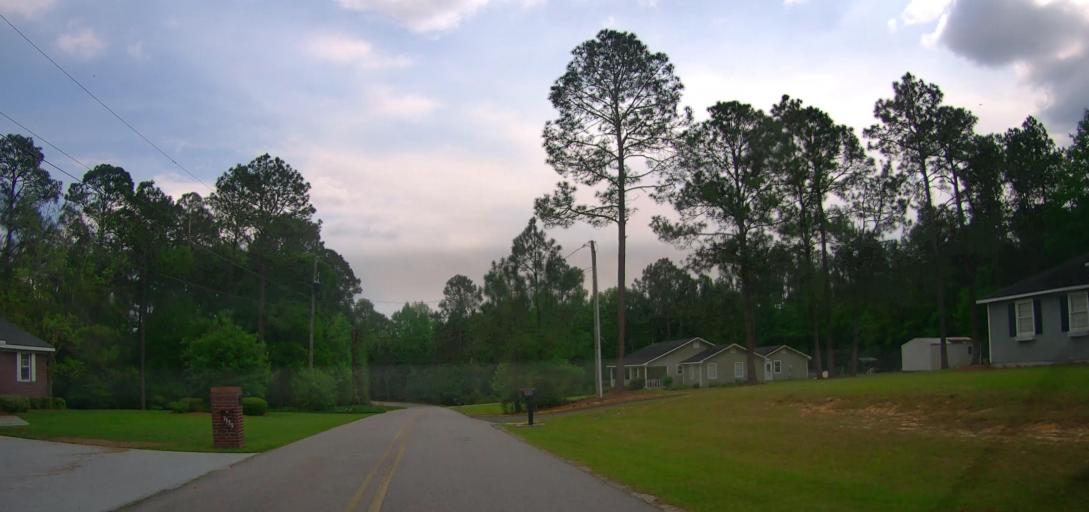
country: US
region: Georgia
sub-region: Treutlen County
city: Soperton
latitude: 32.3638
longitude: -82.5879
